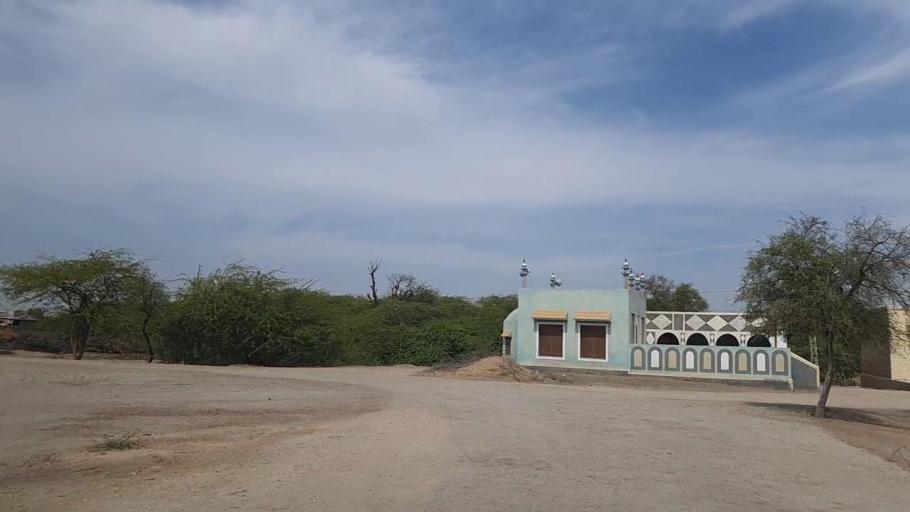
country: PK
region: Sindh
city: Samaro
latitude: 25.2770
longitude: 69.4527
